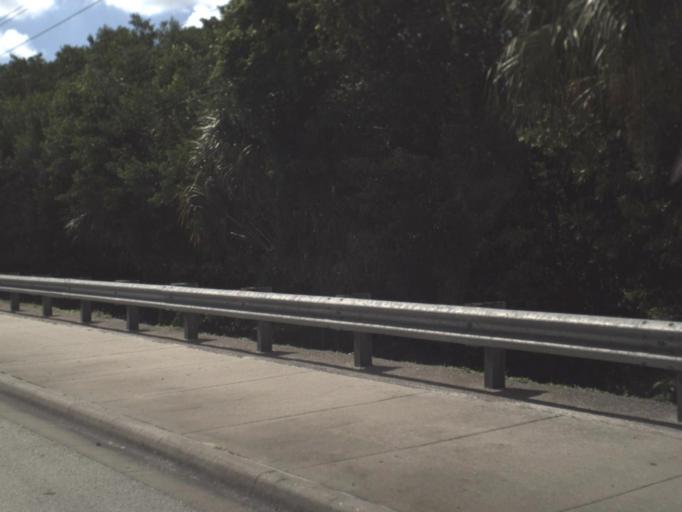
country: US
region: Florida
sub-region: Collier County
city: Naples Park
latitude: 26.2889
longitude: -81.8021
